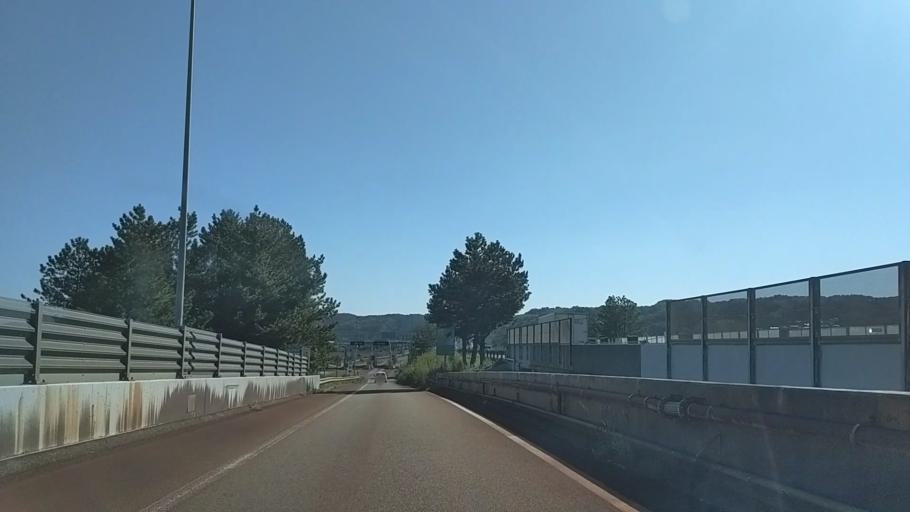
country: JP
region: Ishikawa
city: Kanazawa-shi
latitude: 36.6074
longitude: 136.6742
